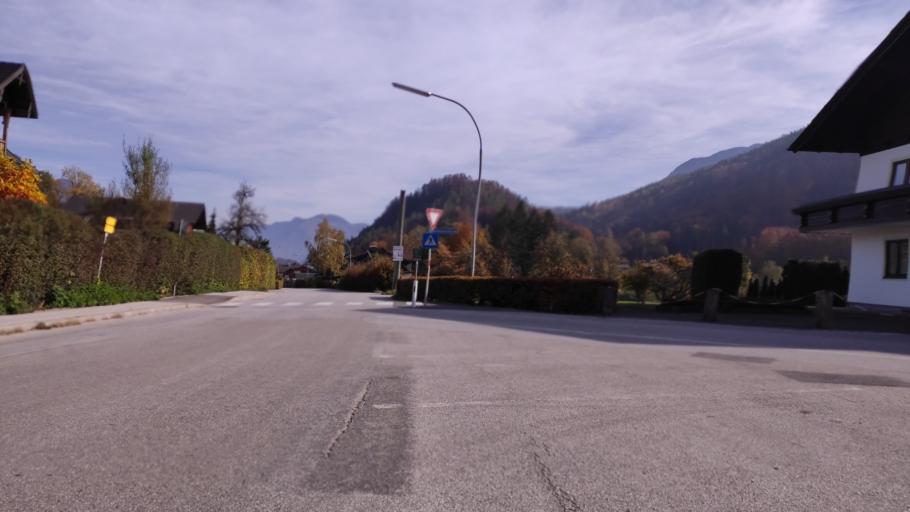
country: AT
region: Salzburg
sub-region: Politischer Bezirk Salzburg-Umgebung
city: Strobl
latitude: 47.7131
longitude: 13.4993
